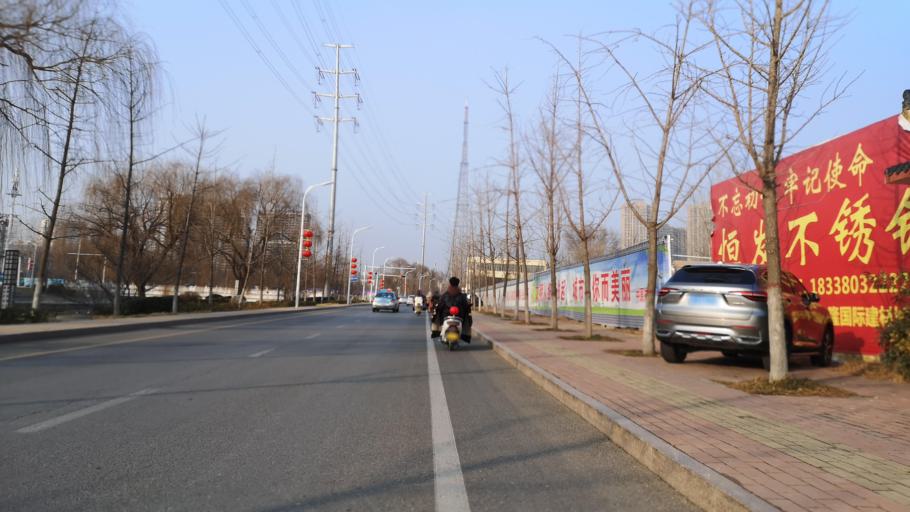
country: CN
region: Henan Sheng
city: Zhongyuanlu
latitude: 35.7744
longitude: 115.0487
